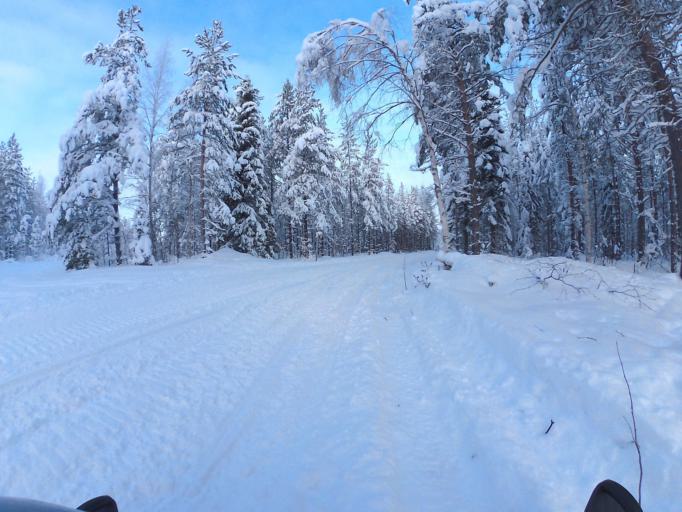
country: FI
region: Lapland
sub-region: Rovaniemi
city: Rovaniemi
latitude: 66.5230
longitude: 26.0210
